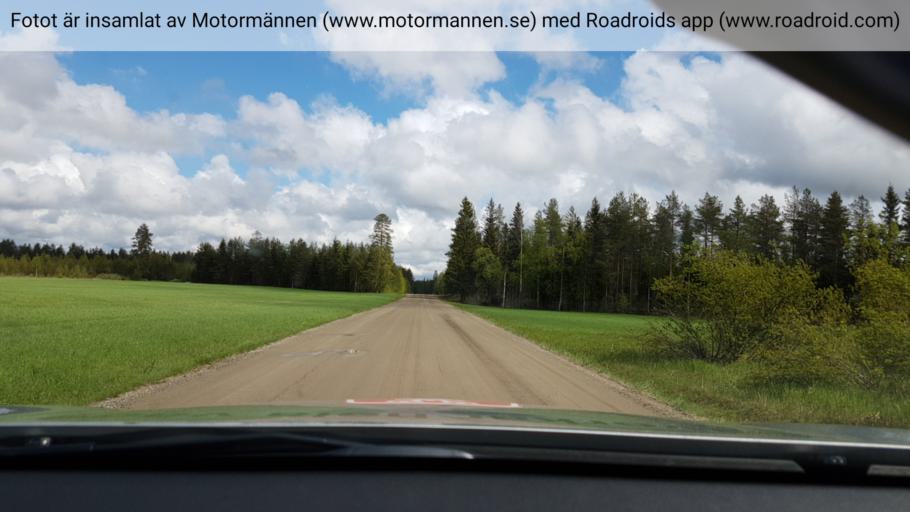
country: SE
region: Vaesterbotten
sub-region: Vindelns Kommun
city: Vindeln
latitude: 64.0805
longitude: 19.6156
